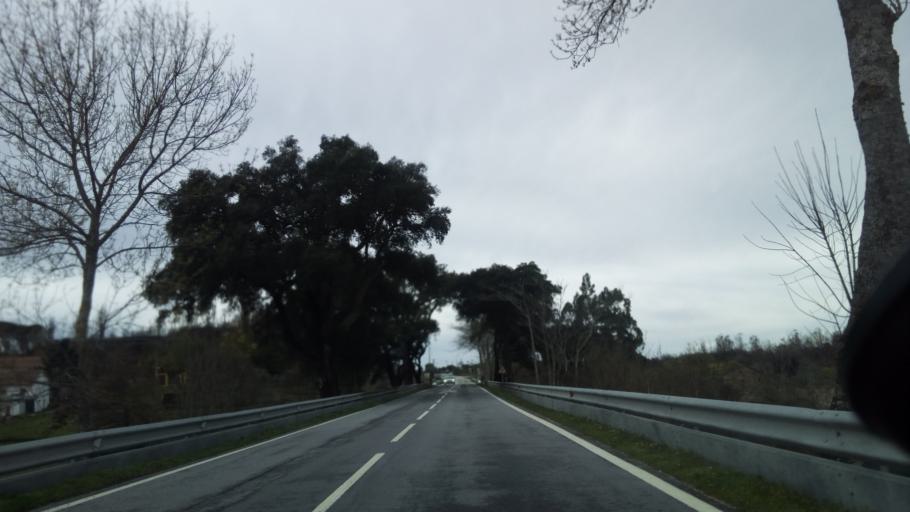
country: PT
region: Guarda
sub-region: Fornos de Algodres
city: Fornos de Algodres
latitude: 40.5218
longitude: -7.6111
